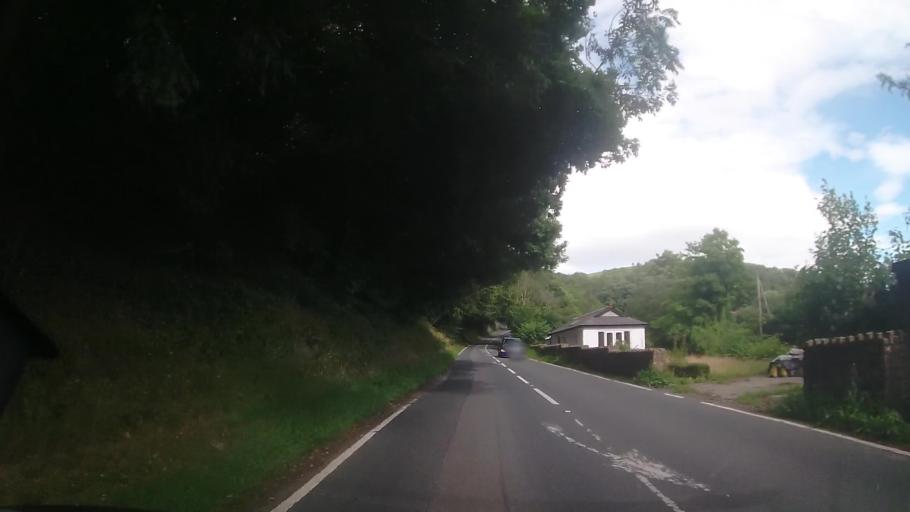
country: GB
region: Wales
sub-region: Denbighshire
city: Llangollen
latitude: 52.9845
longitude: -3.1840
